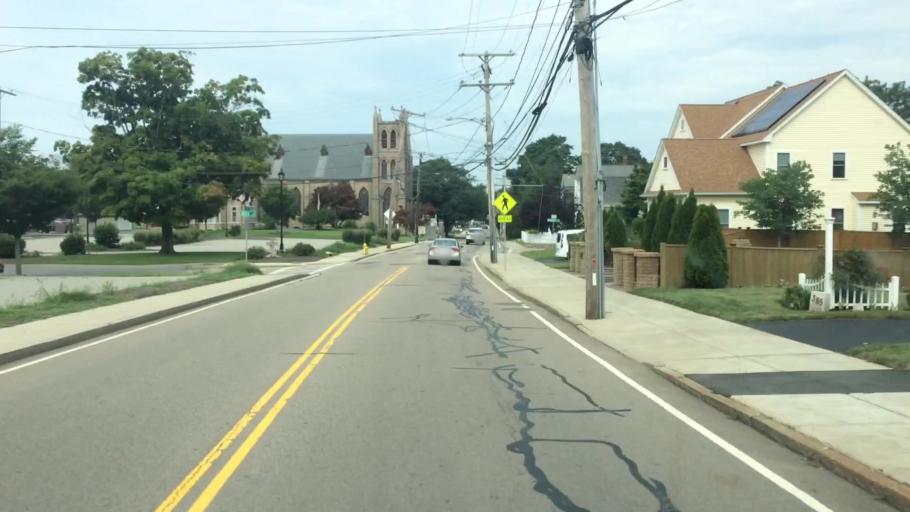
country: US
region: Massachusetts
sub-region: Norfolk County
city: Dedham
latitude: 42.2483
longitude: -71.1644
